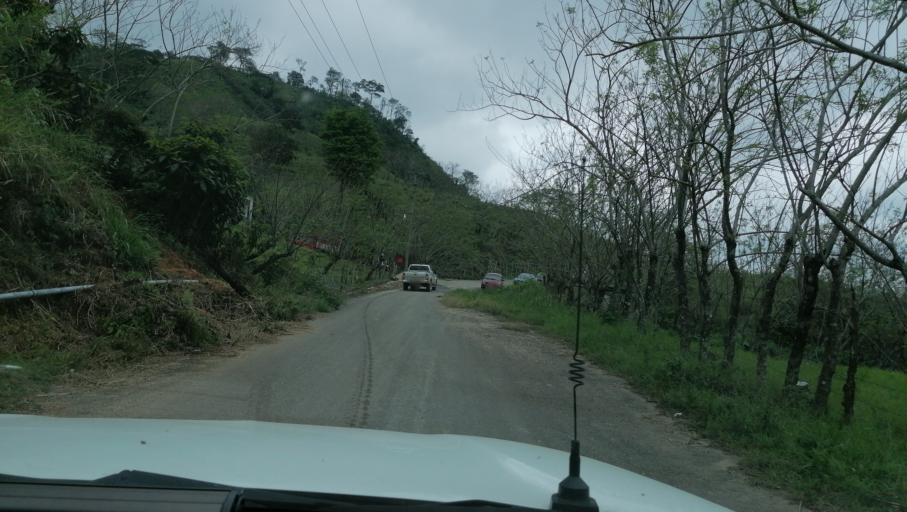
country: MX
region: Chiapas
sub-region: Francisco Leon
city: San Miguel la Sardina
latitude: 17.2727
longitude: -93.2664
